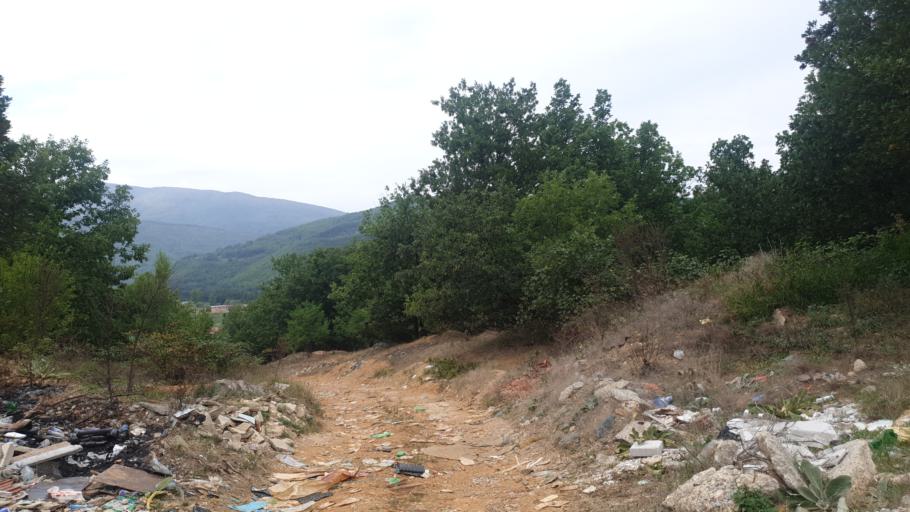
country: MK
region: Kicevo
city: Zajas
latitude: 41.5722
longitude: 20.9469
